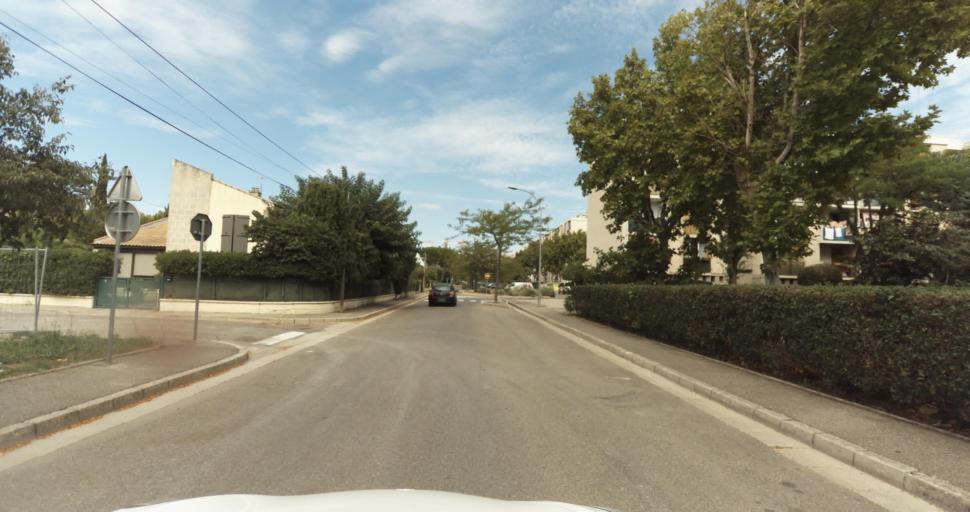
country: FR
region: Provence-Alpes-Cote d'Azur
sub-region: Departement des Bouches-du-Rhone
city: Miramas
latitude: 43.5887
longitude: 5.0040
